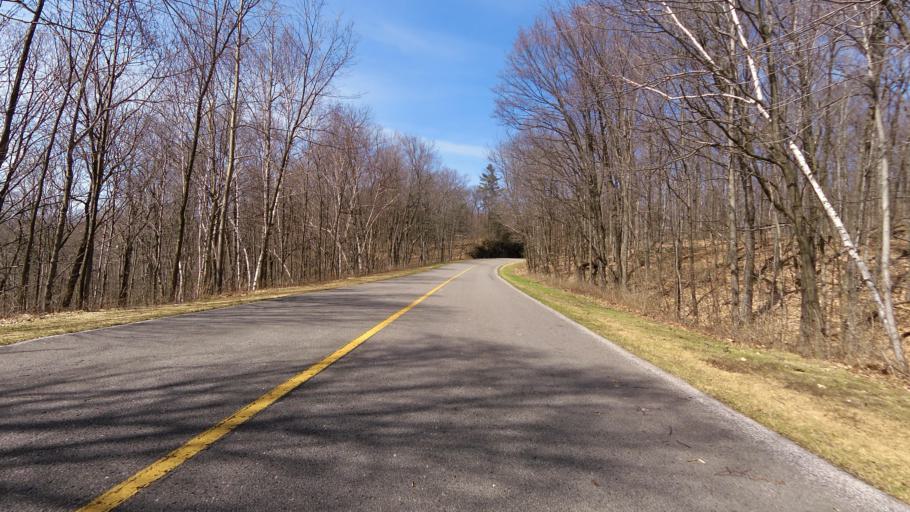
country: CA
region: Quebec
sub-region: Outaouais
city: Gatineau
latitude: 45.4816
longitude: -75.8541
